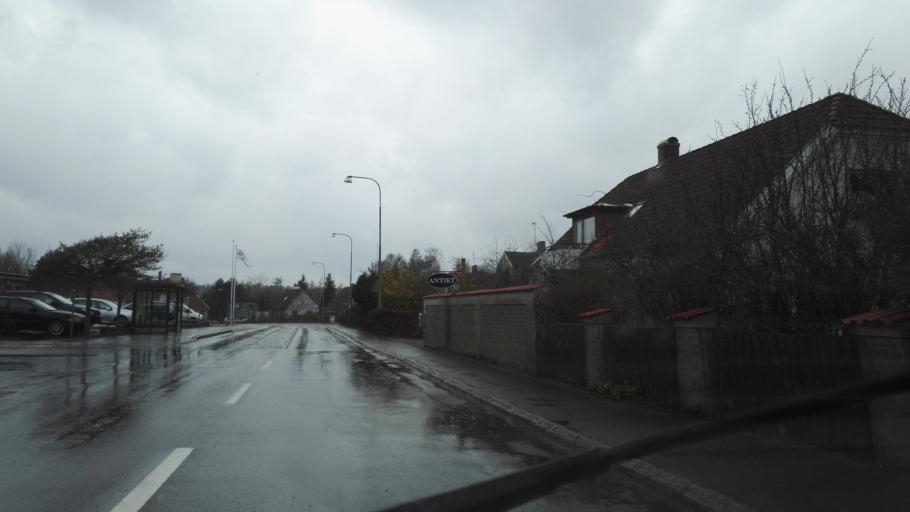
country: SE
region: Skane
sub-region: Kristianstads Kommun
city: Degeberga
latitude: 55.7243
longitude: 14.1092
